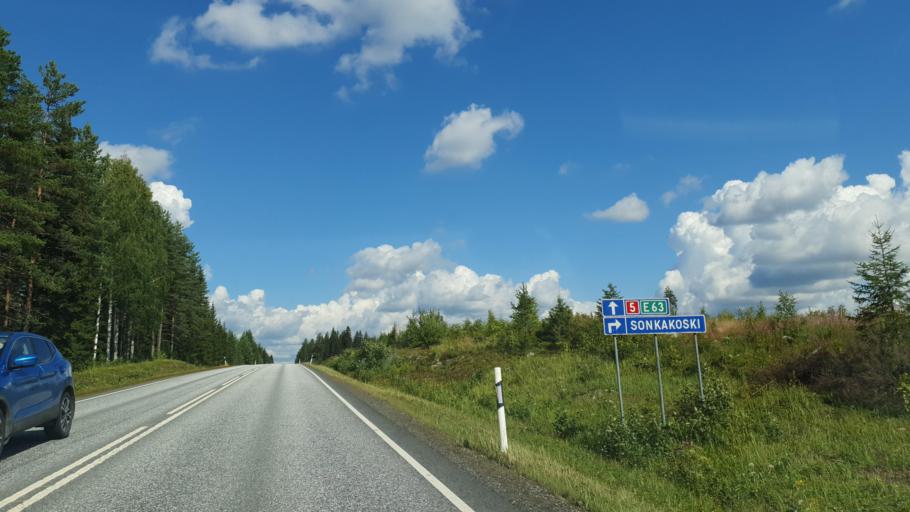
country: FI
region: Northern Savo
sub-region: Ylae-Savo
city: Sonkajaervi
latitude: 63.7741
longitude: 27.4155
